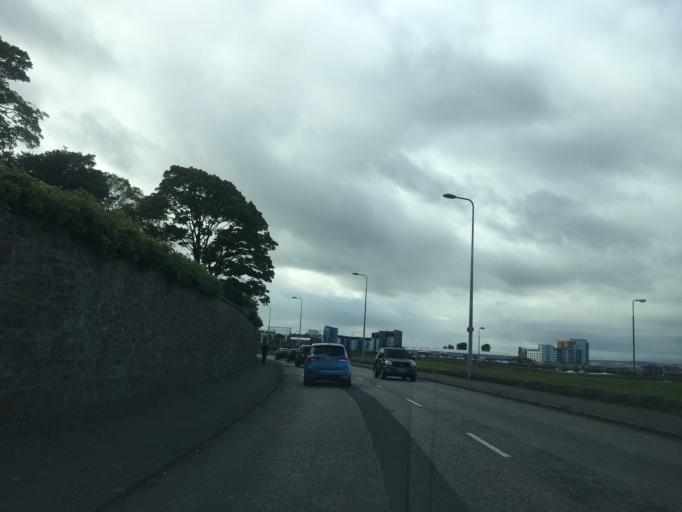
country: GB
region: Scotland
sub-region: Edinburgh
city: Edinburgh
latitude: 55.9805
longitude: -3.2124
